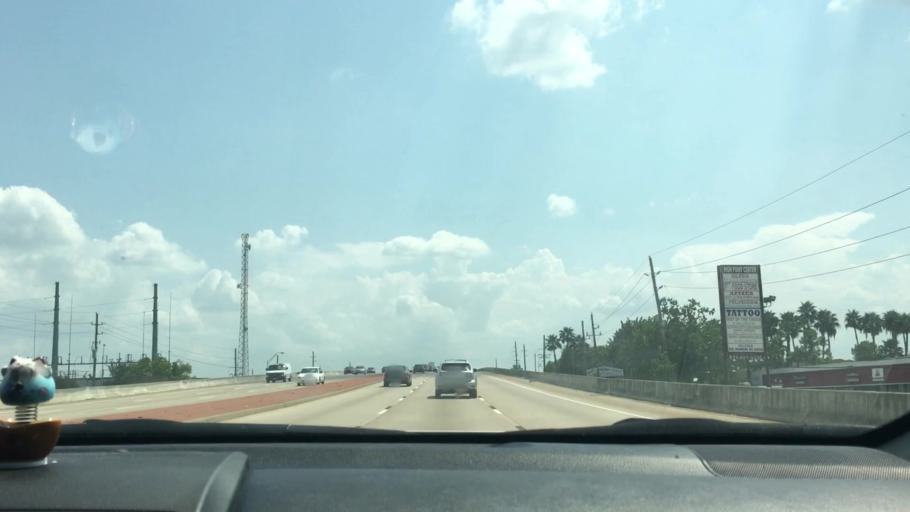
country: US
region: Texas
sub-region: Fort Bend County
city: Mission Bend
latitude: 29.7136
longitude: -95.6442
